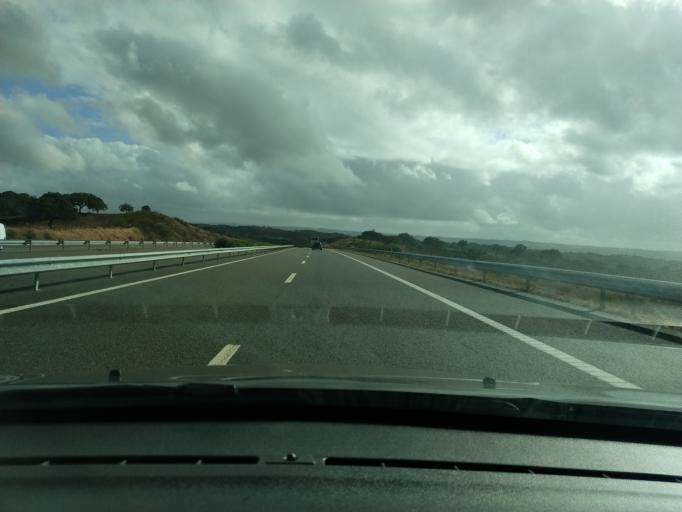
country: PT
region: Beja
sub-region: Ourique
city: Ourique
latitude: 37.5623
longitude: -8.1922
